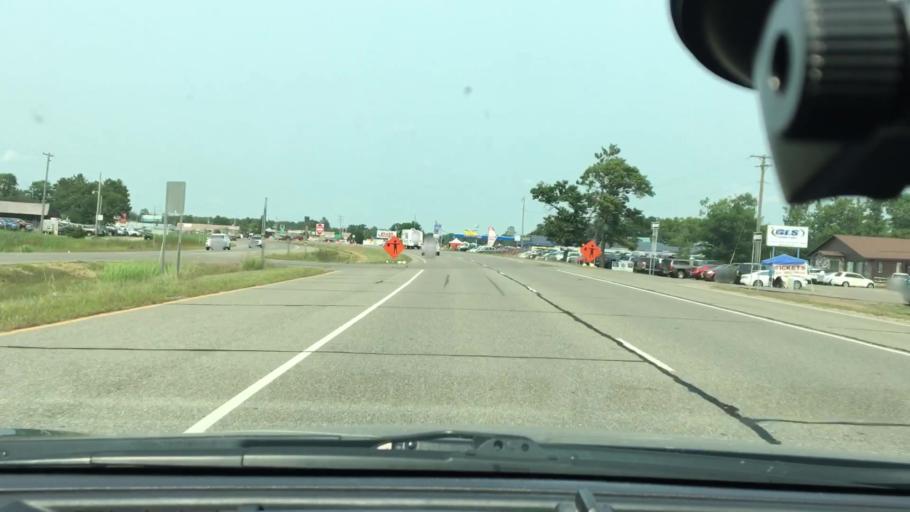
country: US
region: Minnesota
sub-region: Cass County
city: East Gull Lake
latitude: 46.4139
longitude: -94.2856
